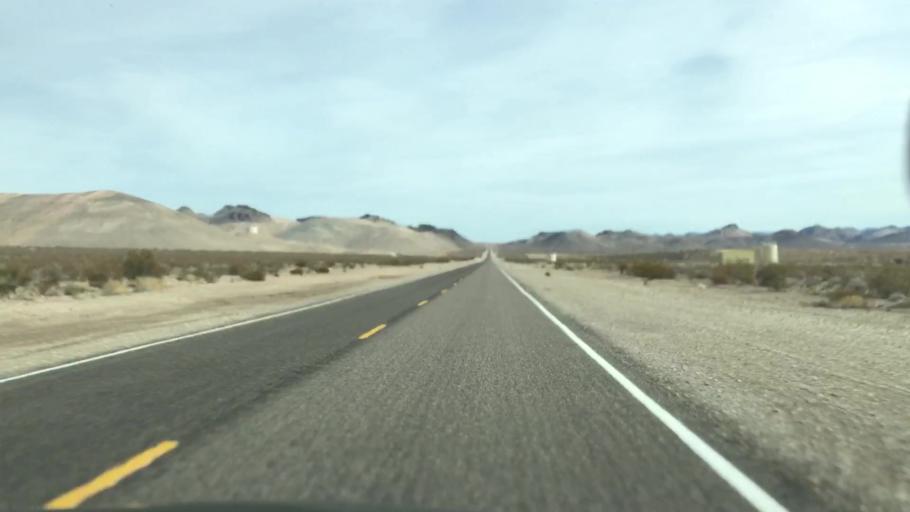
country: US
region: Nevada
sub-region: Nye County
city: Beatty
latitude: 36.8740
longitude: -116.8268
